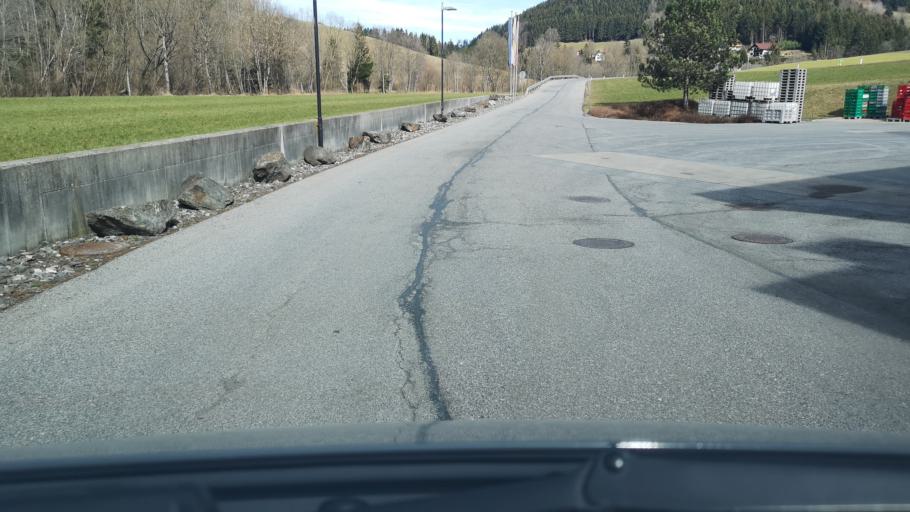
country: AT
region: Styria
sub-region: Politischer Bezirk Weiz
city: Birkfeld
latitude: 47.3659
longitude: 15.6901
